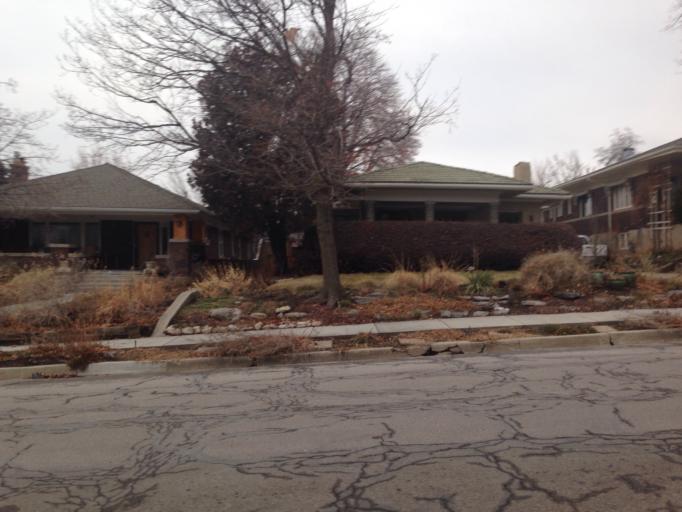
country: US
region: Utah
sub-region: Salt Lake County
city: Salt Lake City
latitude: 40.7458
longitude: -111.8523
